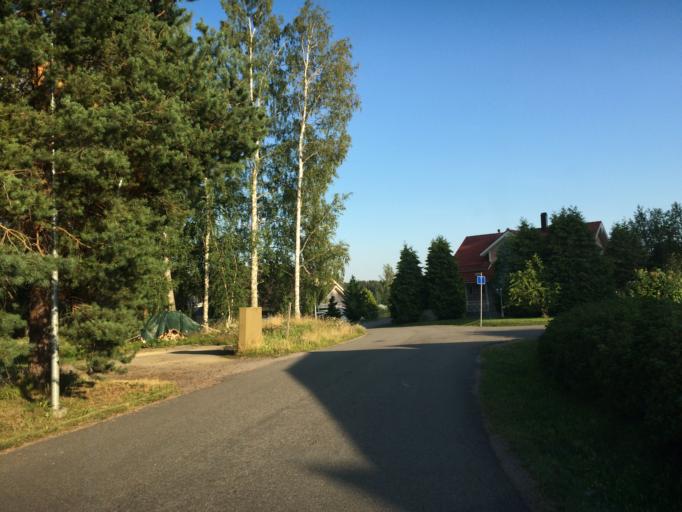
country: FI
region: Haeme
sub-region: Haemeenlinna
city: Parola
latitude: 61.0443
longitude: 24.3820
